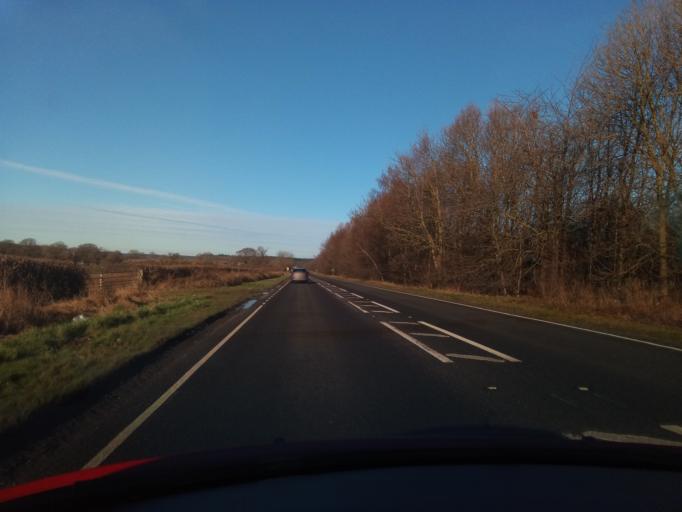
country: GB
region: England
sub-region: Nottinghamshire
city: Burton Joyce
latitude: 53.0438
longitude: -1.0597
